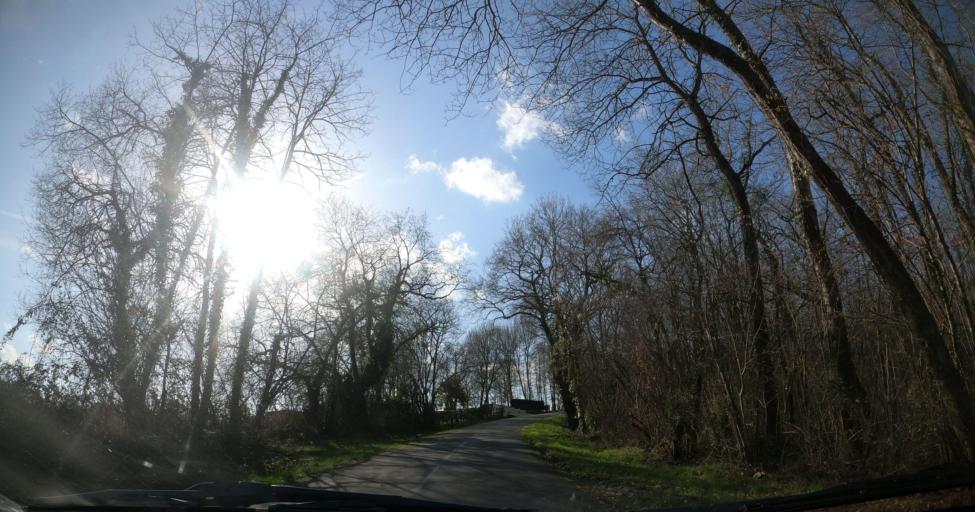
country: FR
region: Aquitaine
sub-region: Departement des Pyrenees-Atlantiques
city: Briscous
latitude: 43.4426
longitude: -1.3702
